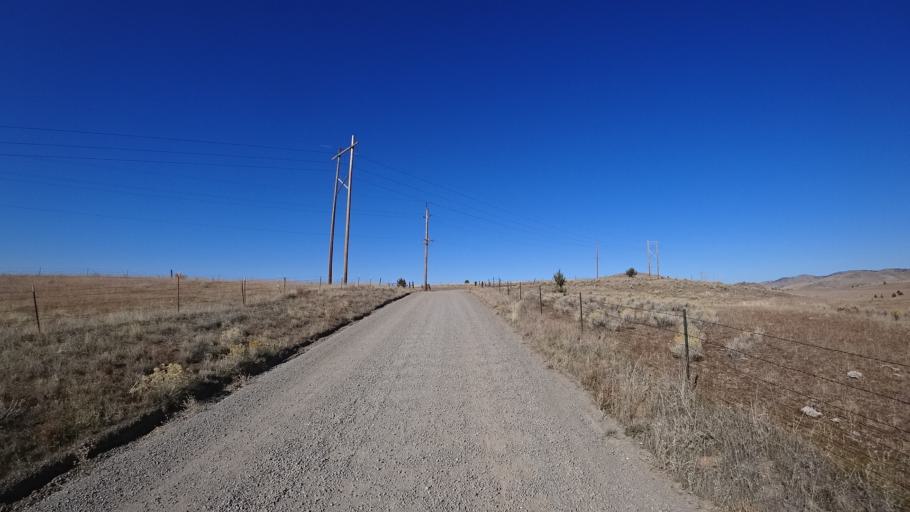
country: US
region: California
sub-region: Siskiyou County
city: Montague
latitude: 41.7690
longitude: -122.3586
